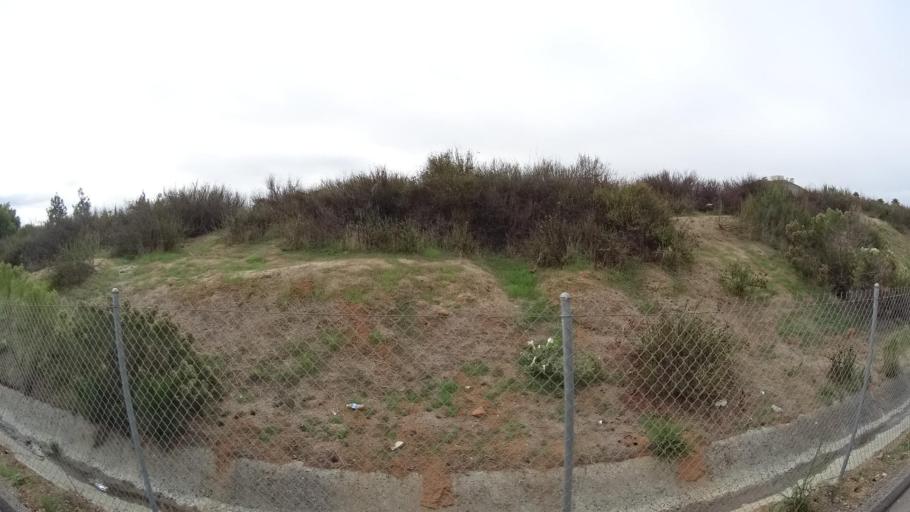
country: US
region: California
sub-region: San Diego County
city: Rancho San Diego
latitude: 32.7640
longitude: -116.9244
